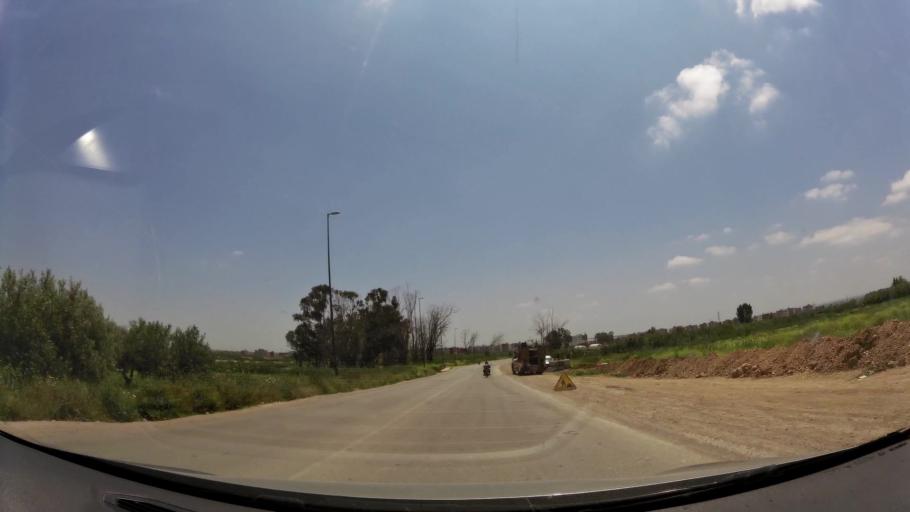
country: MA
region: Fes-Boulemane
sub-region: Fes
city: Fes
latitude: 34.0409
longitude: -5.0617
